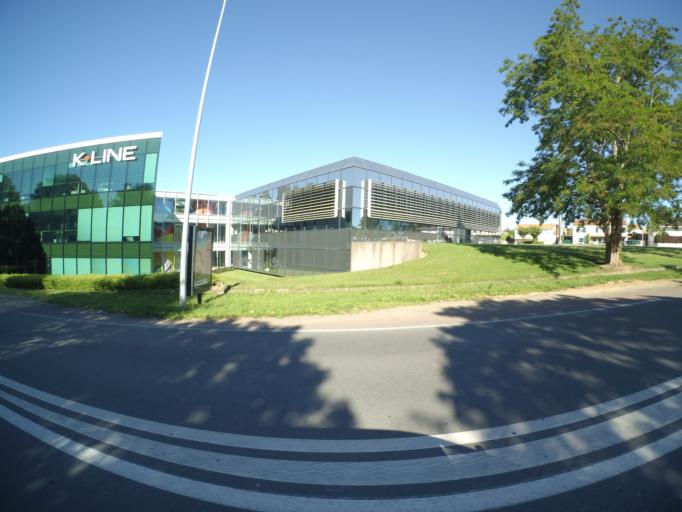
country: FR
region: Pays de la Loire
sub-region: Departement de la Vendee
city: Les Herbiers
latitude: 46.8676
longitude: -1.0264
